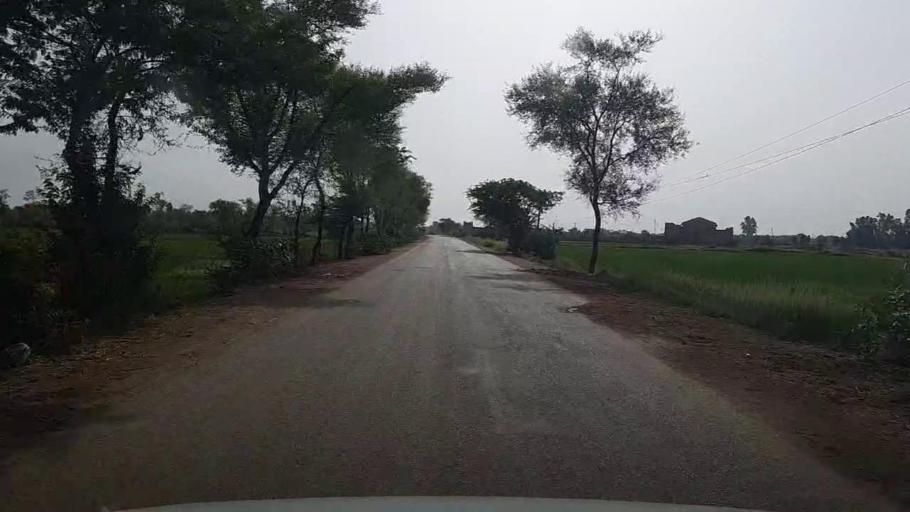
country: PK
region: Sindh
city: Mehar
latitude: 27.1206
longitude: 67.8129
